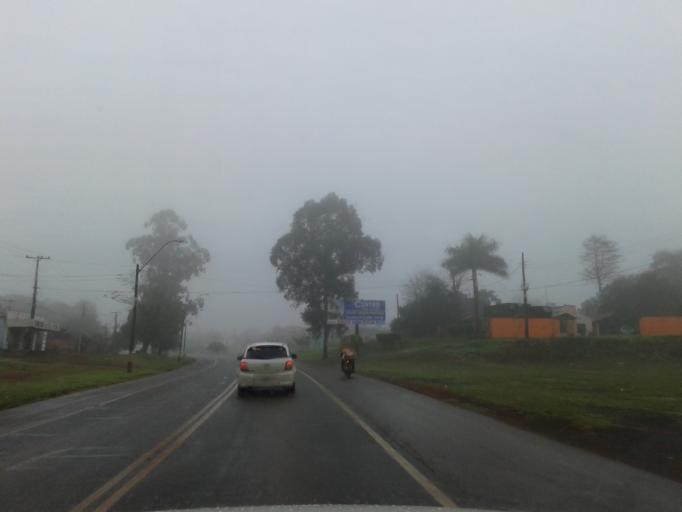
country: PY
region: Itapua
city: Arquitecto Tomas Romero Pereira
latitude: -26.5441
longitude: -55.2559
